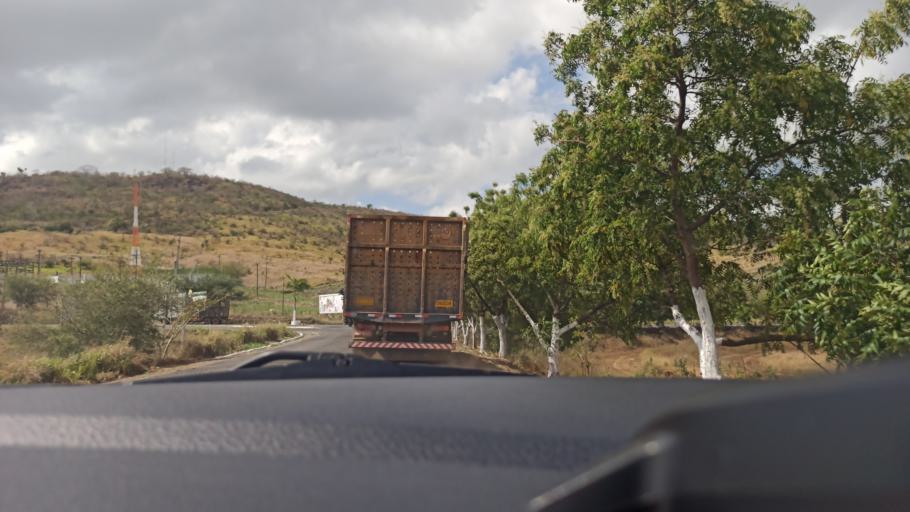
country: BR
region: Pernambuco
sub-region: Timbauba
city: Timbauba
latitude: -7.5201
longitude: -35.3053
